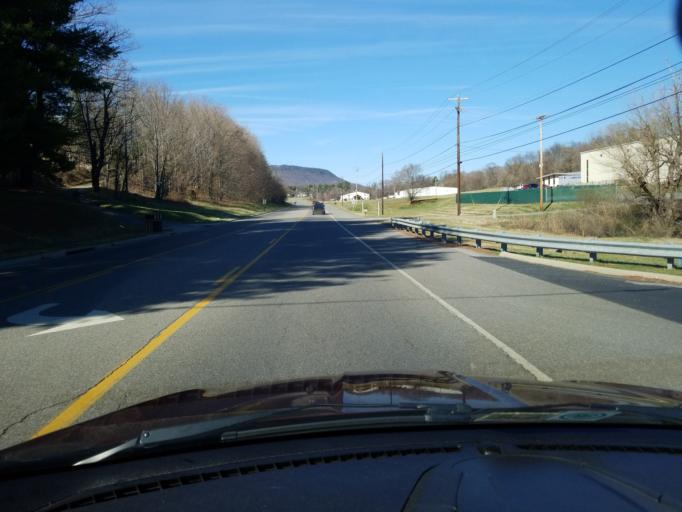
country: US
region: Virginia
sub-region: Roanoke County
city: Hollins
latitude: 37.3322
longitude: -79.9268
